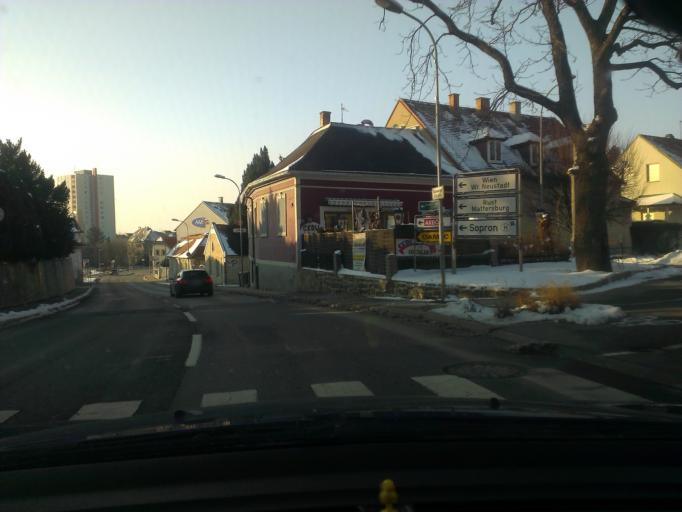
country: AT
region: Burgenland
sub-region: Eisenstadt Stadt
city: Eisenstadt
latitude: 47.8447
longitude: 16.5261
